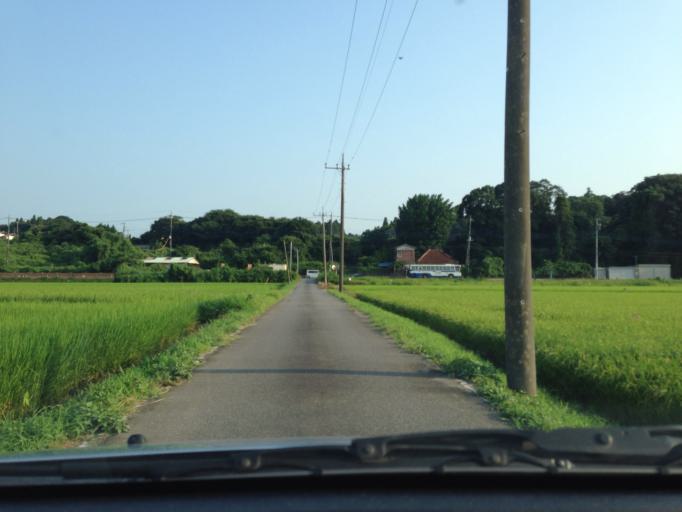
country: JP
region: Ibaraki
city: Ami
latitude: 36.0327
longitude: 140.2662
